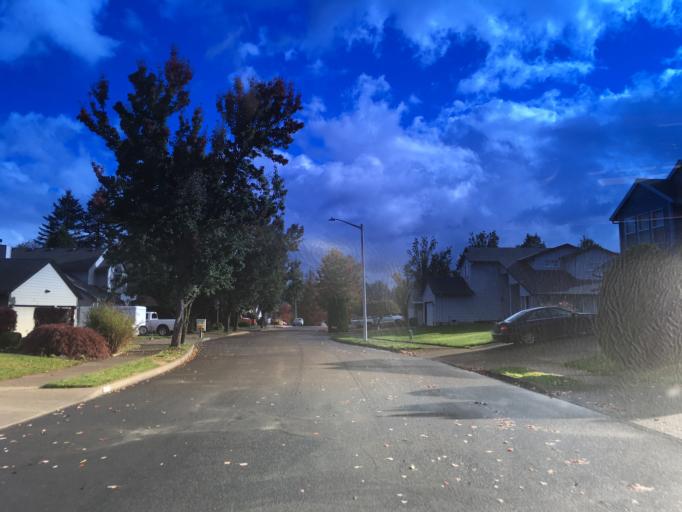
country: US
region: Oregon
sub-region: Multnomah County
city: Troutdale
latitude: 45.5115
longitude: -122.3839
